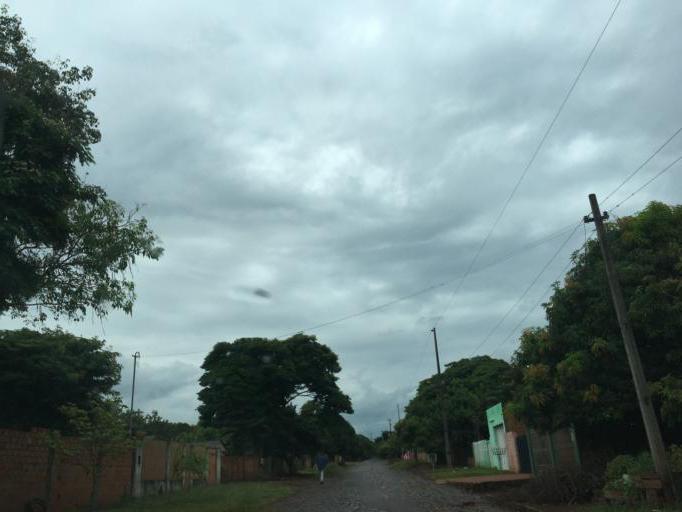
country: PY
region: Alto Parana
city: Ciudad del Este
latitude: -25.4372
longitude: -54.6519
